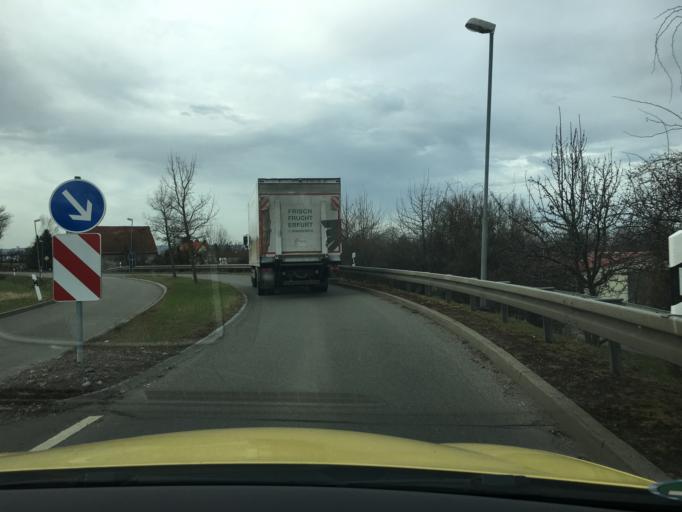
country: DE
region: Thuringia
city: Ollendorf
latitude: 51.0395
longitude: 11.1930
